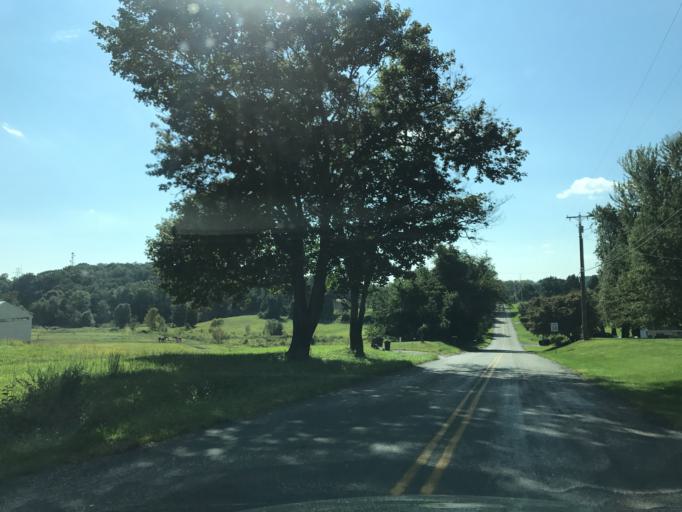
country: US
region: Pennsylvania
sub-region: York County
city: Stewartstown
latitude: 39.6940
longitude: -76.5307
